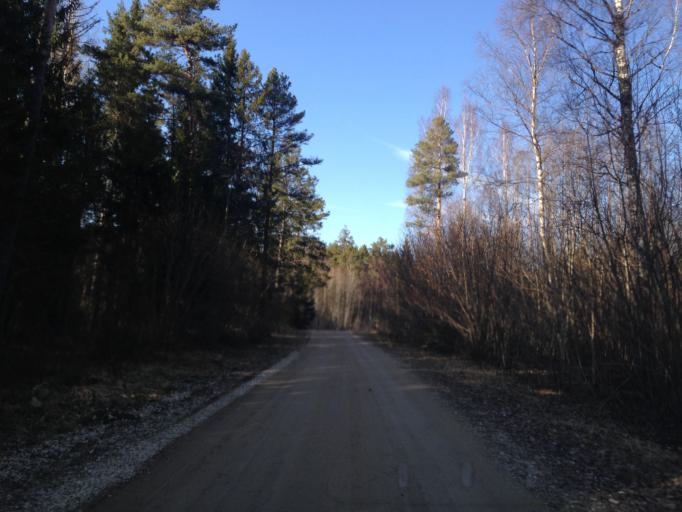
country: EE
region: Harju
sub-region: Nissi vald
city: Turba
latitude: 59.1312
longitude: 24.1650
